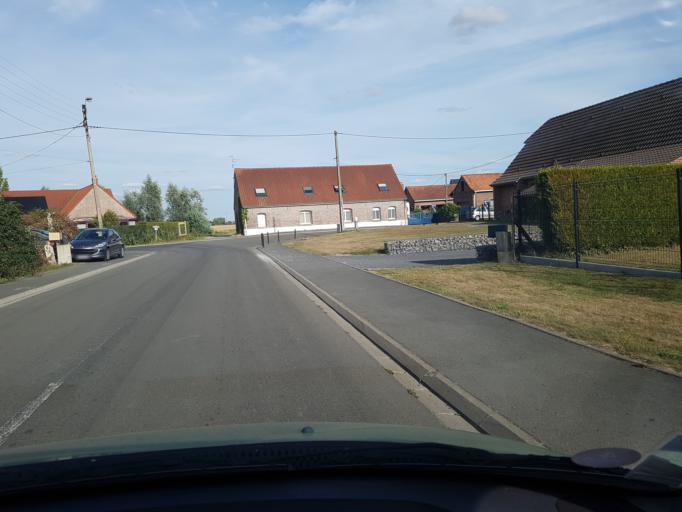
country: FR
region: Nord-Pas-de-Calais
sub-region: Departement du Pas-de-Calais
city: Lestrem
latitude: 50.6058
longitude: 2.7027
